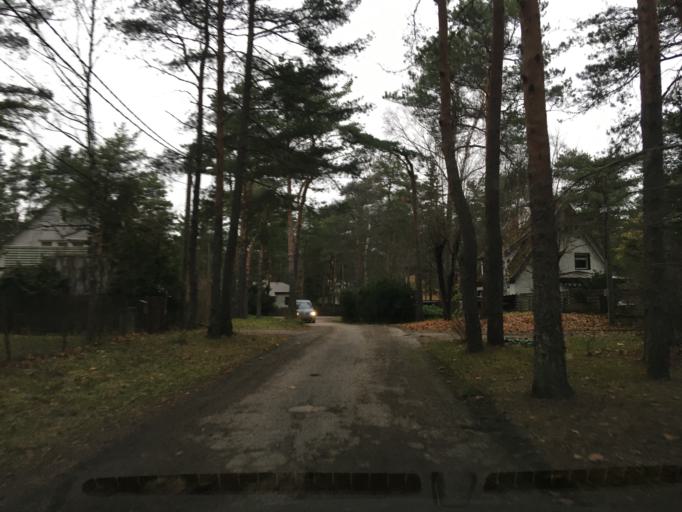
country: EE
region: Harju
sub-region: Saku vald
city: Saku
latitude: 59.3725
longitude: 24.6952
